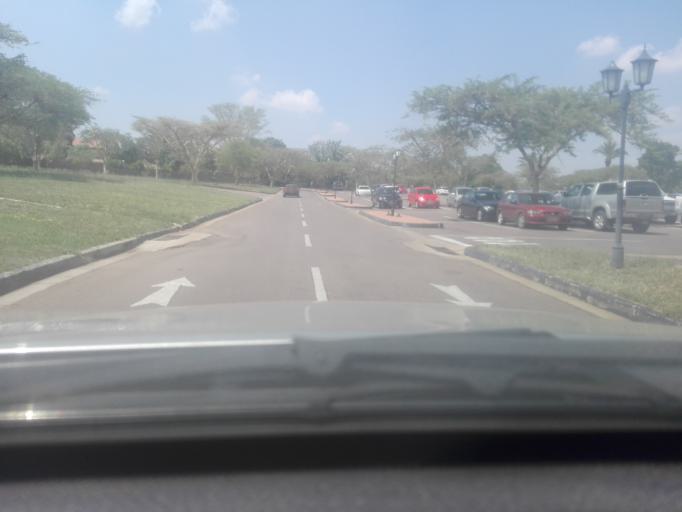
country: BW
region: Kweneng
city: Mogoditshane
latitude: -24.6397
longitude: 25.8759
